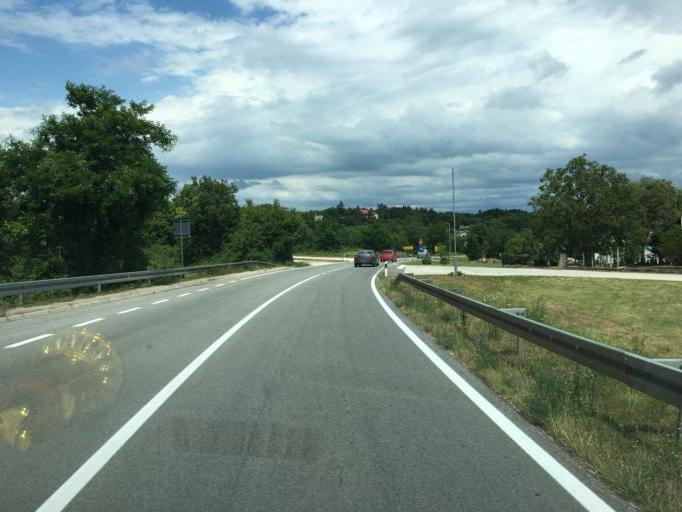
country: HR
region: Istarska
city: Karojba
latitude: 45.2204
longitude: 13.8353
